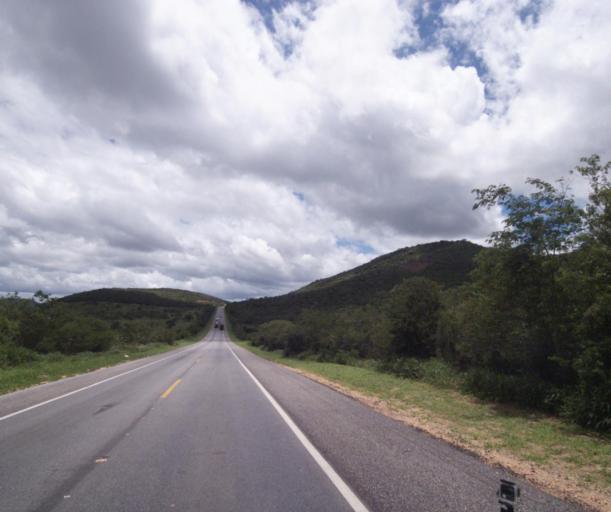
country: BR
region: Bahia
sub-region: Pocoes
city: Pocoes
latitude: -14.3748
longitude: -40.3472
